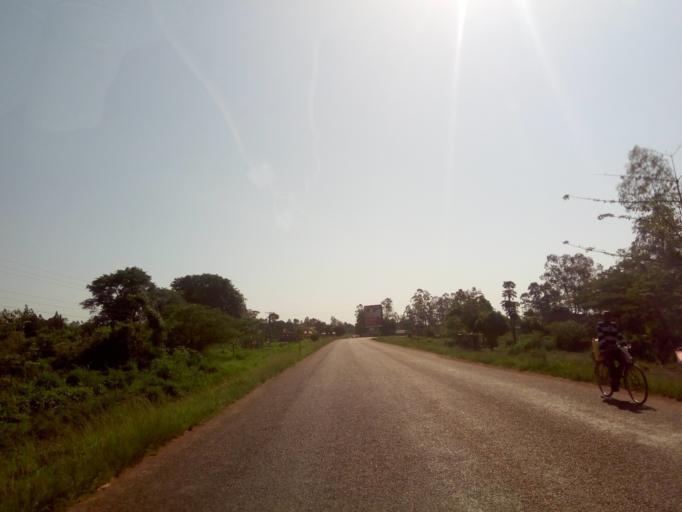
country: UG
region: Western Region
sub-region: Masindi District
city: Masindi
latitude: 1.6708
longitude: 31.7507
